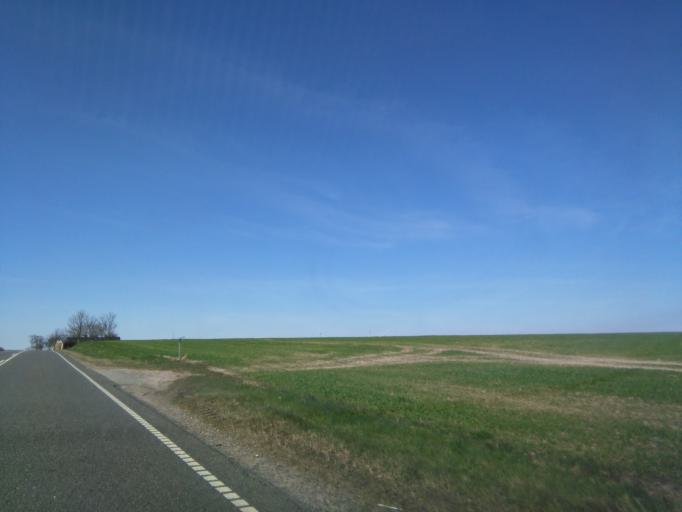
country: DK
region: Central Jutland
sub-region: Skanderborg Kommune
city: Skanderborg
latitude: 56.0289
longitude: 9.8700
